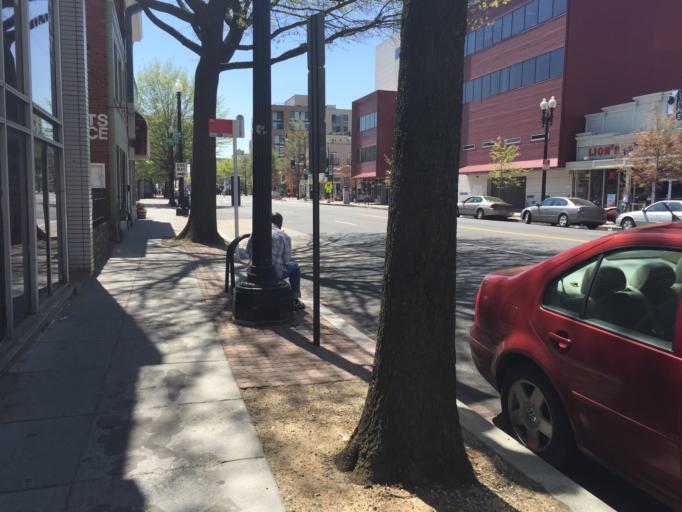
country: US
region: Washington, D.C.
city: Washington, D.C.
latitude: 38.9350
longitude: -77.0239
